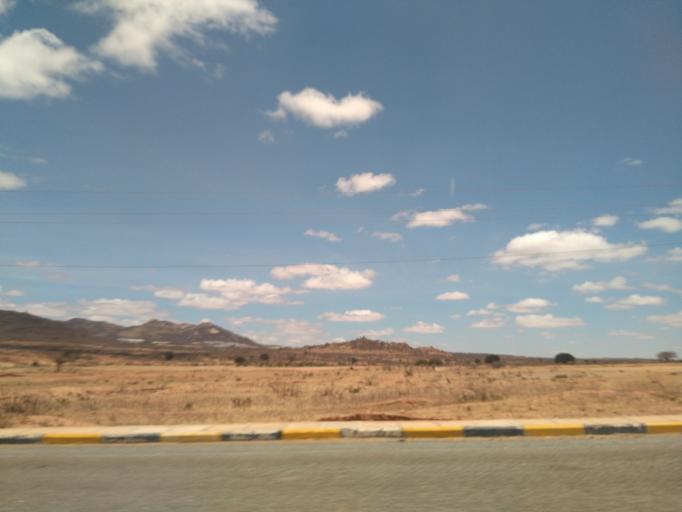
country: TZ
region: Dodoma
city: Kisasa
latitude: -6.2005
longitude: 35.8237
